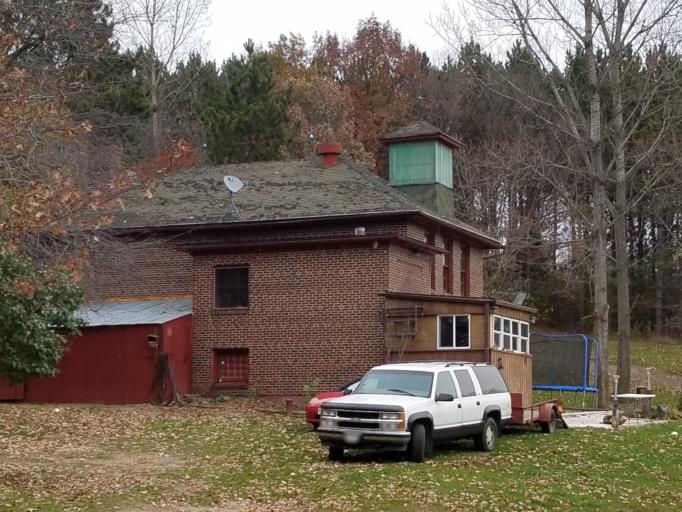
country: US
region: Wisconsin
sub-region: Vernon County
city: Hillsboro
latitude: 43.6088
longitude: -90.3491
